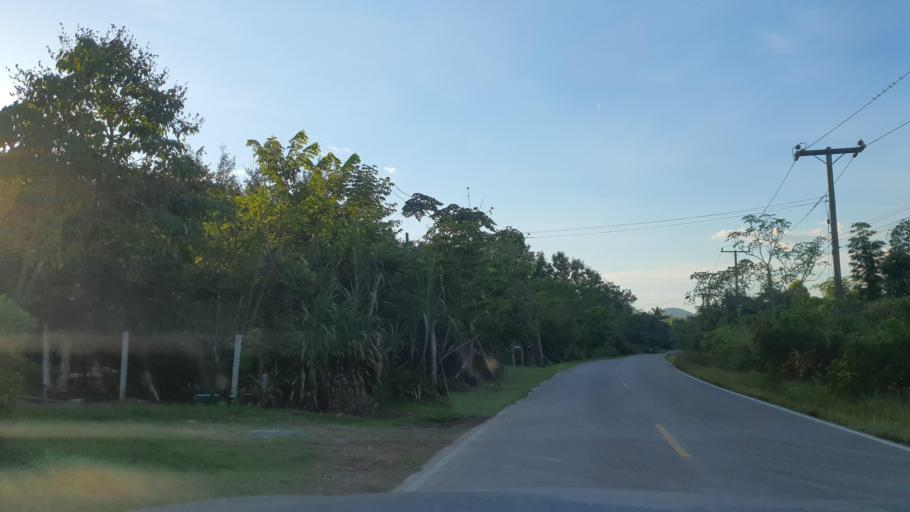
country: TH
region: Chiang Mai
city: Mae On
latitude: 18.8349
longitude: 99.2832
